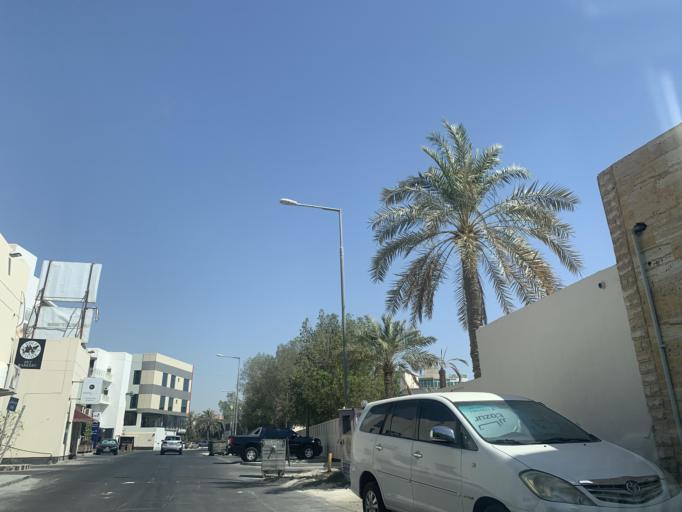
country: BH
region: Manama
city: Jidd Hafs
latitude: 26.2217
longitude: 50.5019
